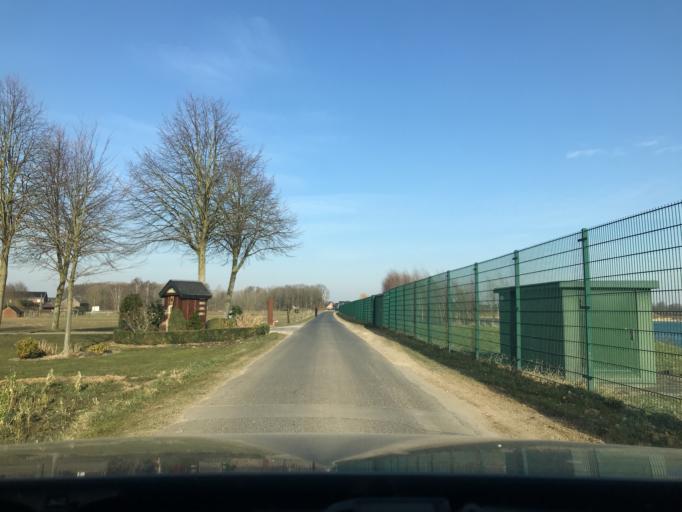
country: DE
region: North Rhine-Westphalia
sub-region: Regierungsbezirk Dusseldorf
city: Wachtendonk
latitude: 51.3976
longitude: 6.3557
